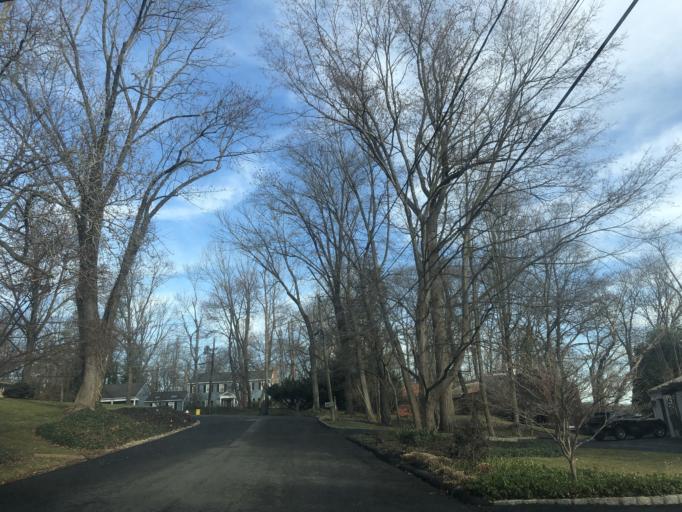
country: US
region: New Jersey
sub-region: Somerset County
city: Kingston
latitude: 40.3567
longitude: -74.6277
